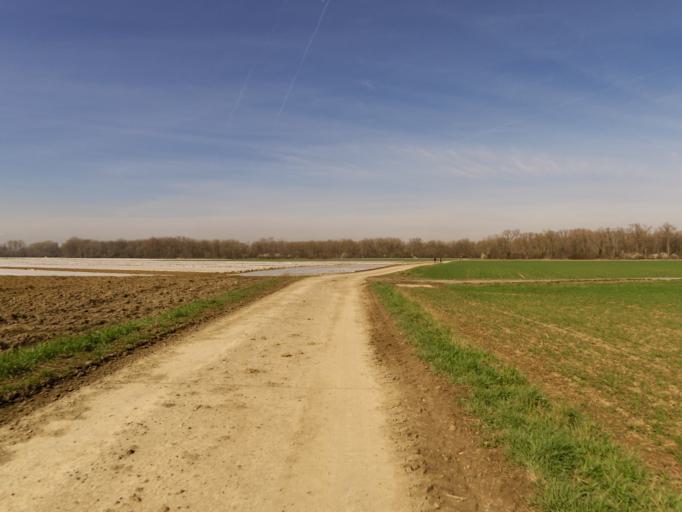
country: DE
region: Hesse
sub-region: Regierungsbezirk Darmstadt
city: Gross-Rohrheim
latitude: 49.7346
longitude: 8.4716
